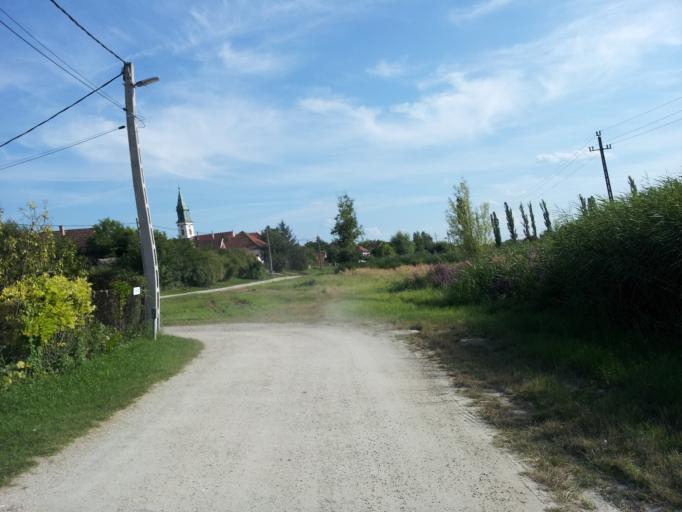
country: HU
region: Pest
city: Kiskunlachaza
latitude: 47.1950
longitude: 19.0047
